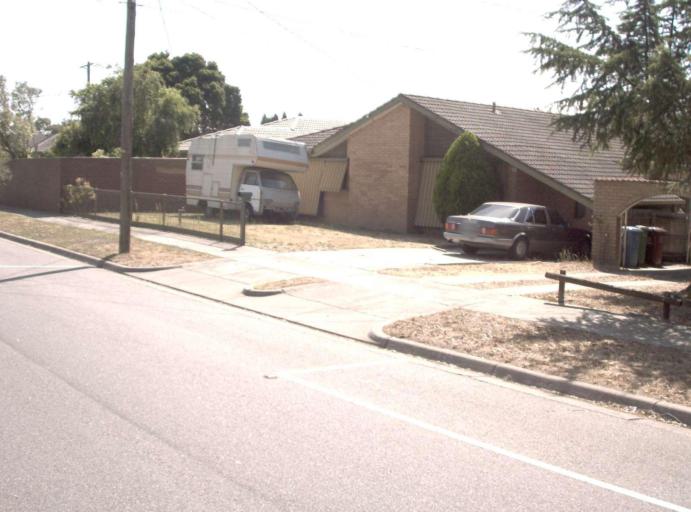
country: AU
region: Victoria
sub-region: Greater Dandenong
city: Noble Park North
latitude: -37.9516
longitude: 145.1914
